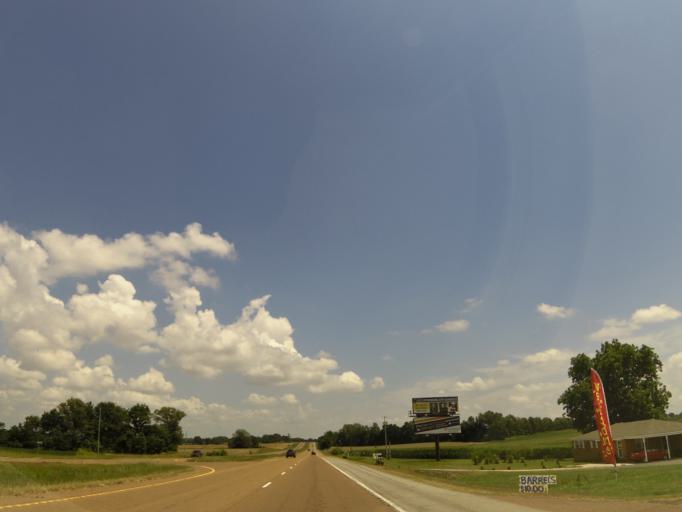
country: US
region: Tennessee
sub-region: Lauderdale County
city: Halls
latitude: 35.9467
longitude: -89.3071
